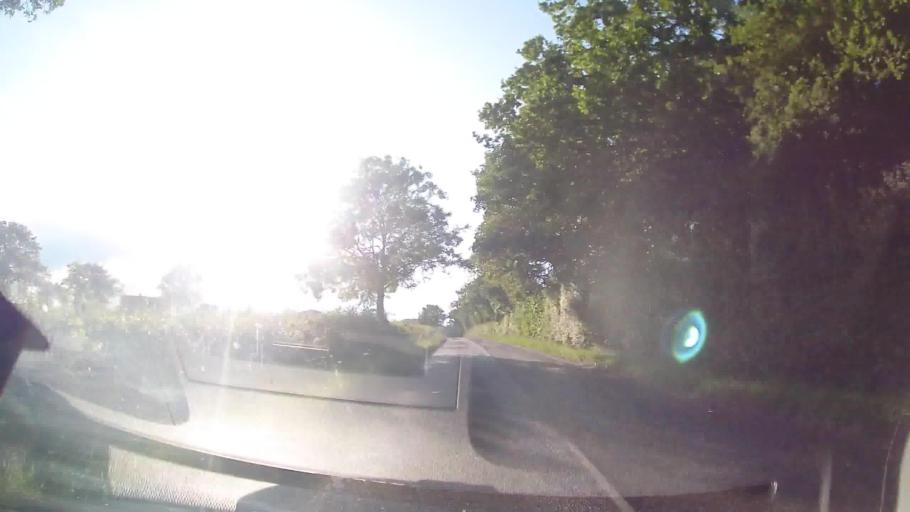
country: GB
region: England
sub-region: Leicestershire
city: Markfield
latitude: 52.6570
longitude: -1.2598
